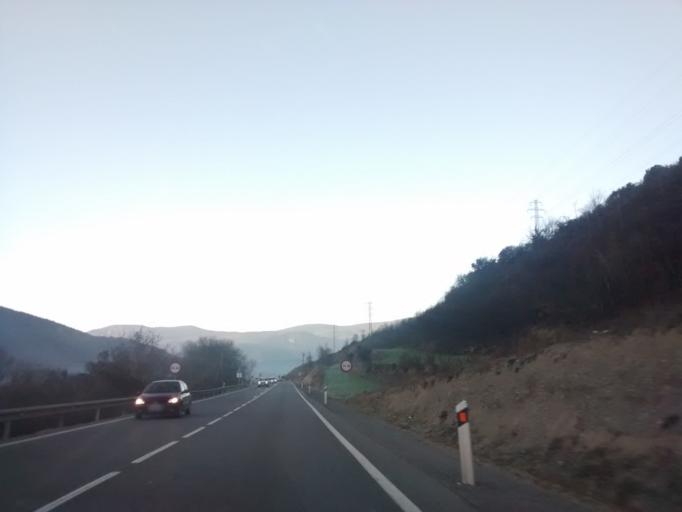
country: ES
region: Catalonia
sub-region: Provincia de Lleida
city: la Seu d'Urgell
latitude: 42.3338
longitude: 1.4094
